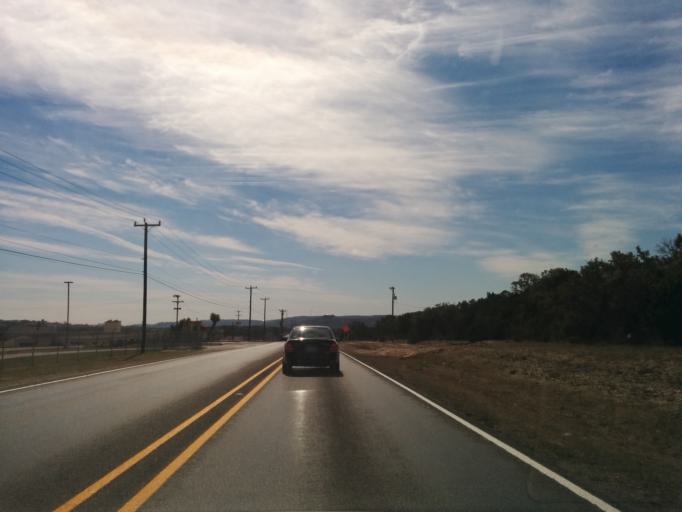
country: US
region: Texas
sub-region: Bexar County
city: Cross Mountain
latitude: 29.6855
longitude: -98.6315
